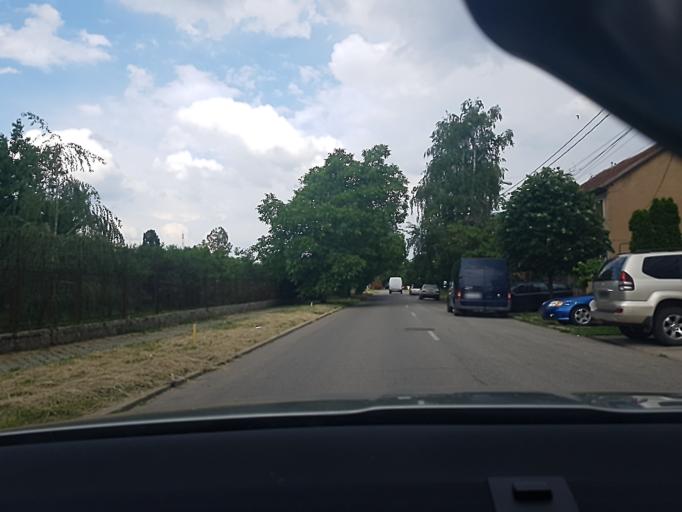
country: RO
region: Timis
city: Timisoara
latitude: 45.7358
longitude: 21.2216
